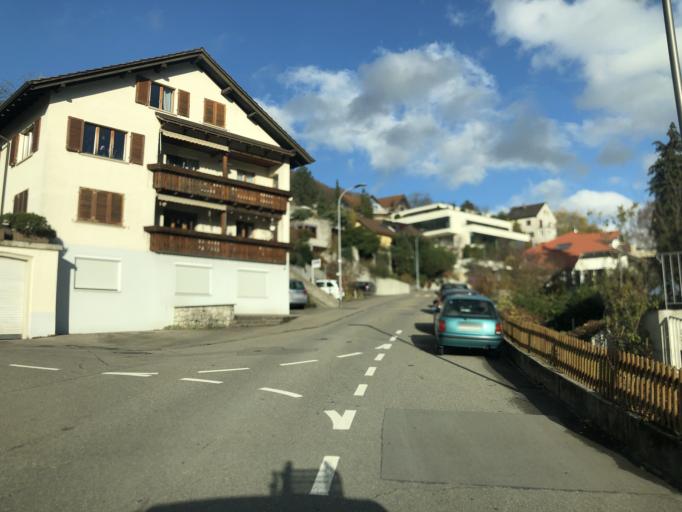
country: CH
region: Aargau
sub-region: Bezirk Baden
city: Wettingen
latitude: 47.4819
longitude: 8.3210
